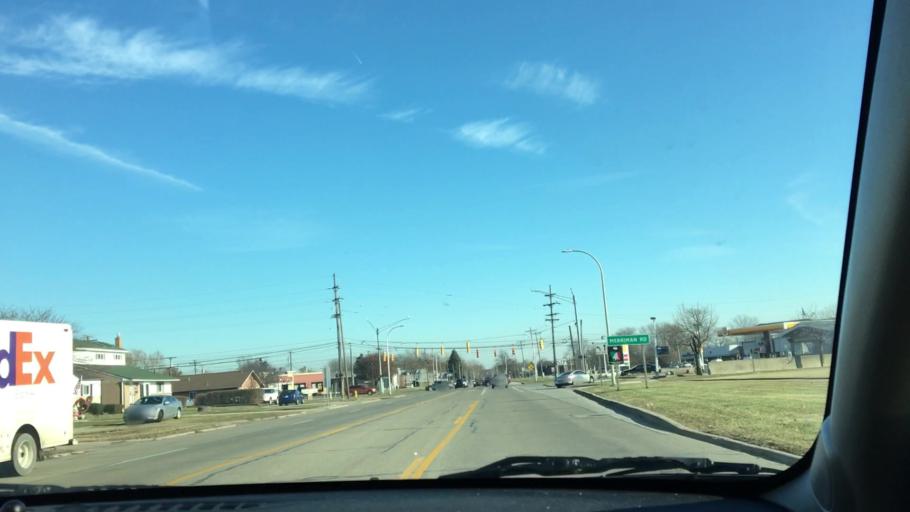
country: US
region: Michigan
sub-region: Wayne County
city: Livonia
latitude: 42.3467
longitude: -83.3528
